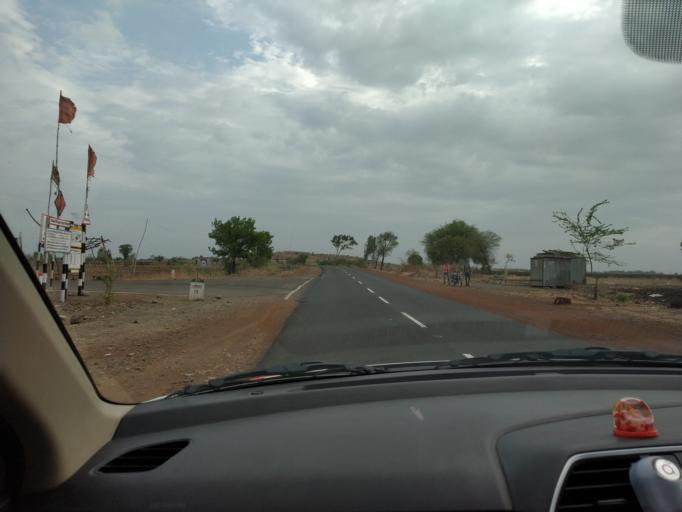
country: IN
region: Madhya Pradesh
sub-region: Shajapur
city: Agar
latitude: 23.6431
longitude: 75.9774
